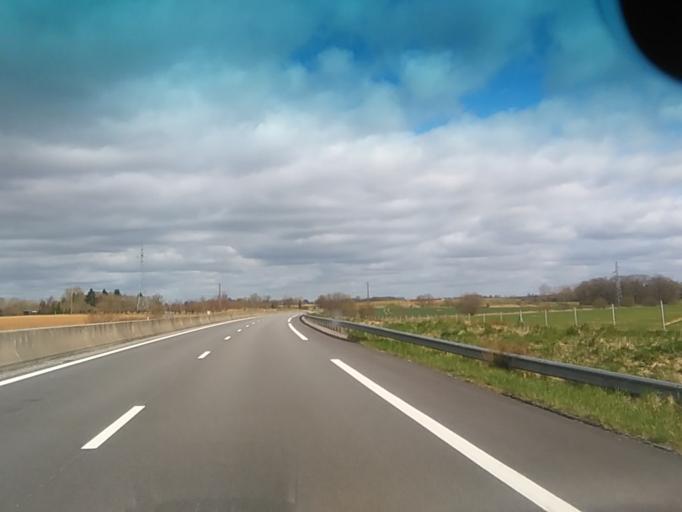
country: FR
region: Haute-Normandie
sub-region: Departement de l'Eure
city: Bernay
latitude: 49.1324
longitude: 0.5362
